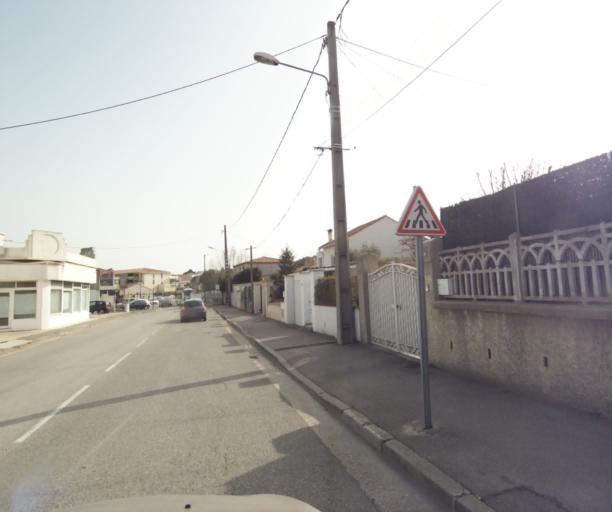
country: FR
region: Provence-Alpes-Cote d'Azur
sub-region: Departement des Bouches-du-Rhone
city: Marseille 15
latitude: 43.3811
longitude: 5.3472
